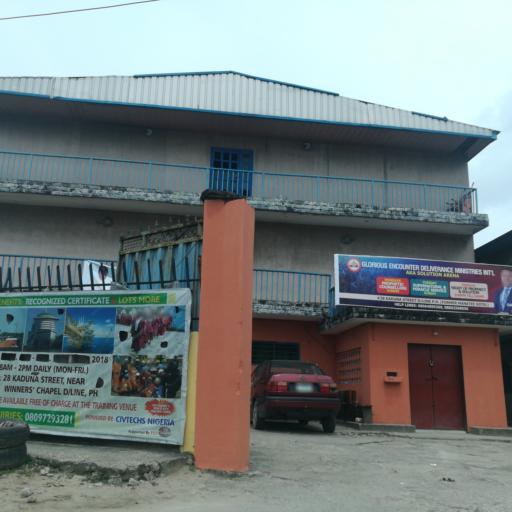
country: NG
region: Rivers
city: Port Harcourt
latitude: 4.7983
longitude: 7.0021
